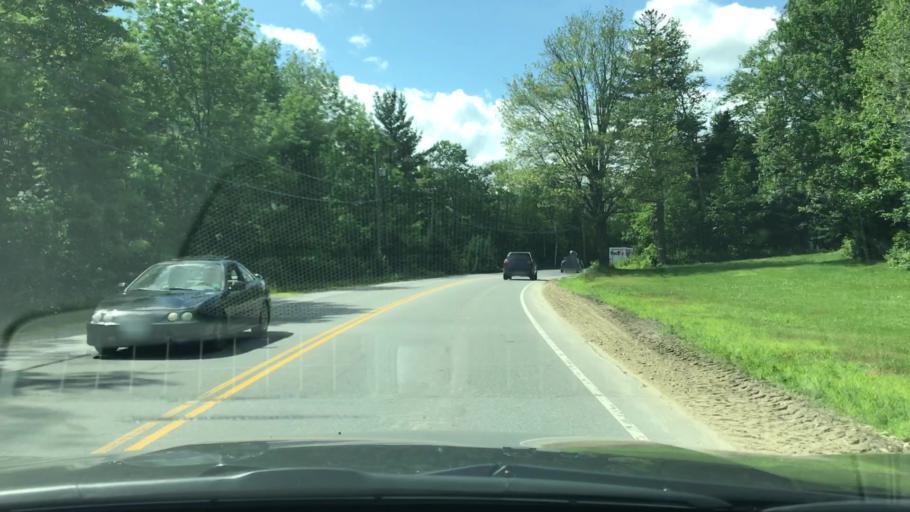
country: US
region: New Hampshire
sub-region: Coos County
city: Jefferson
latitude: 44.3634
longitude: -71.3897
